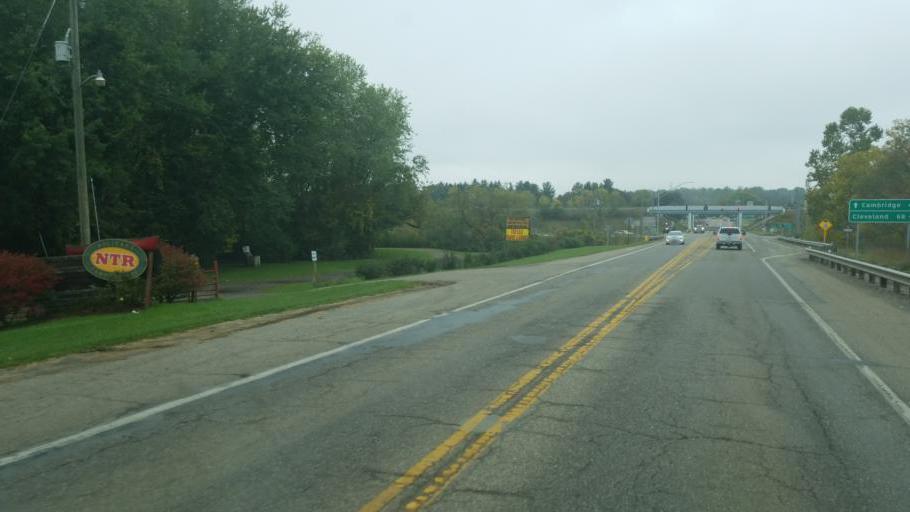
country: US
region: Ohio
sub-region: Tuscarawas County
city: Strasburg
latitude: 40.6429
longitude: -81.4494
